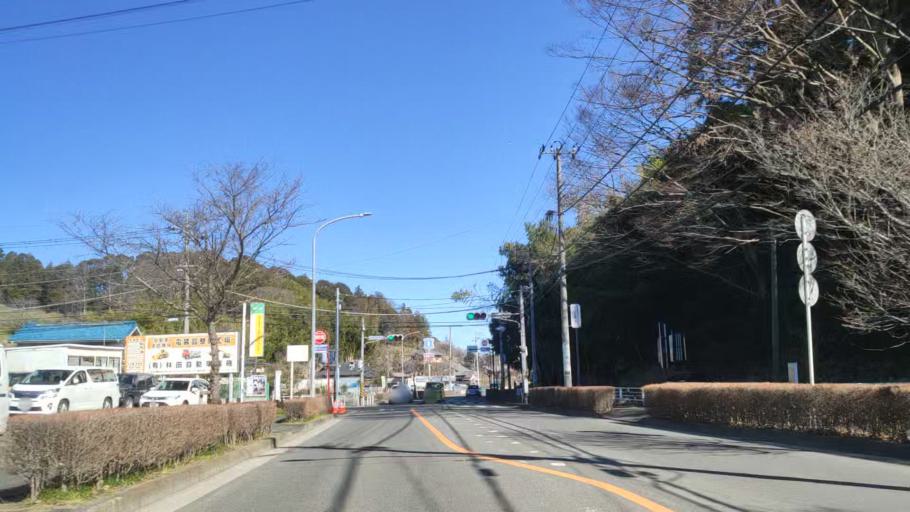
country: JP
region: Kanagawa
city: Minami-rinkan
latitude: 35.5053
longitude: 139.5165
